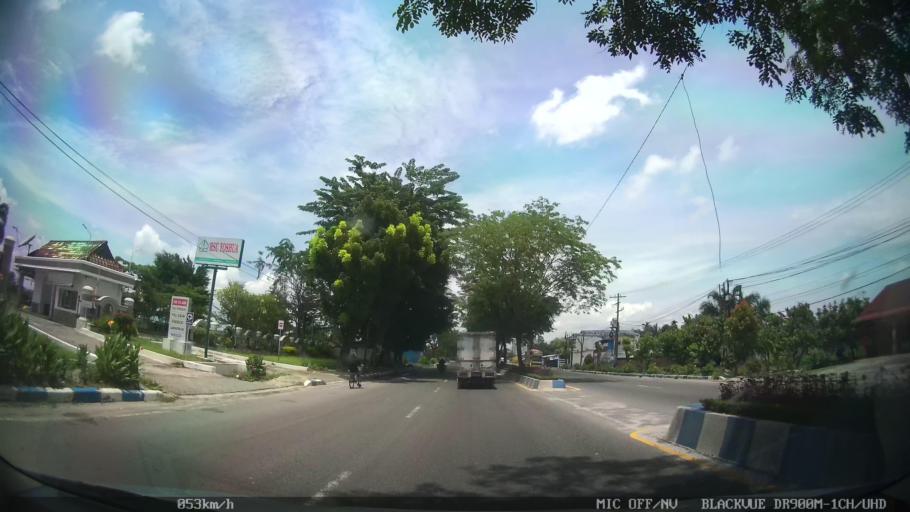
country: ID
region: North Sumatra
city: Percut
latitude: 3.5519
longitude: 98.8605
